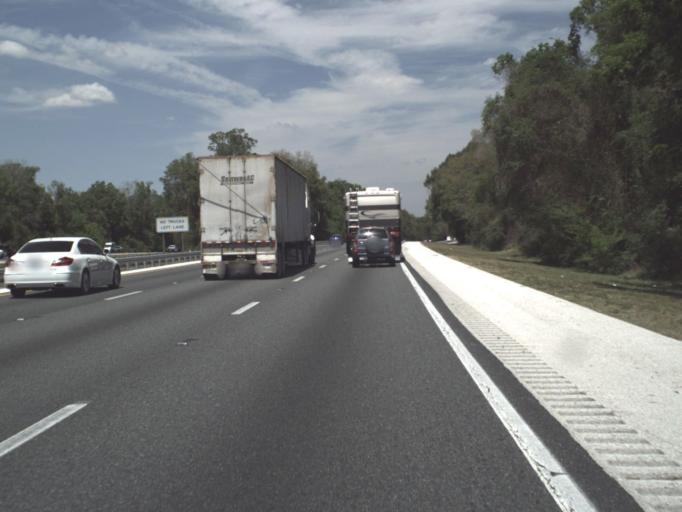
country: US
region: Florida
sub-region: Sumter County
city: Wildwood
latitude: 28.9107
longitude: -82.1094
